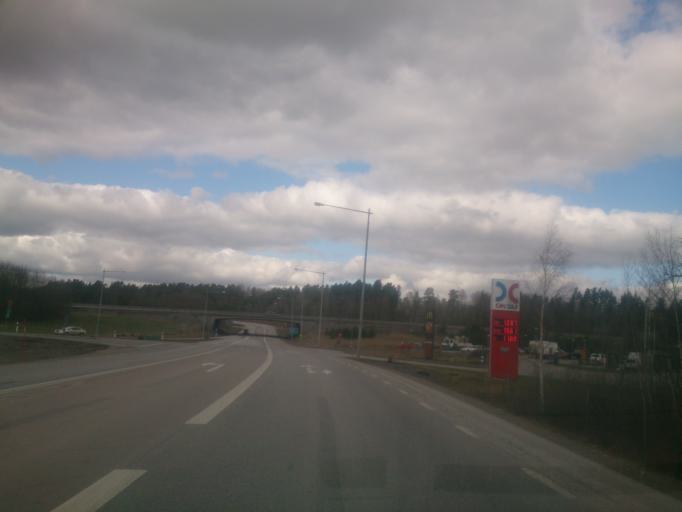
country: SE
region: OEstergoetland
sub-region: Norrkopings Kommun
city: Norrkoping
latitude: 58.5675
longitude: 16.0791
